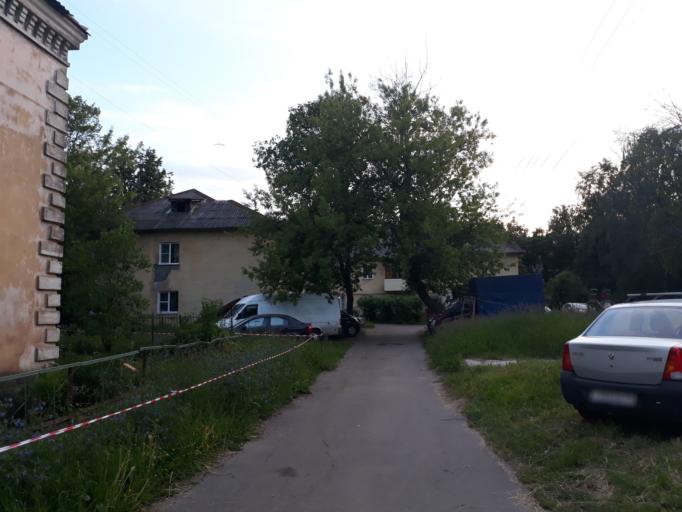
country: RU
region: Jaroslavl
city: Yaroslavl
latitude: 57.6410
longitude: 39.8317
